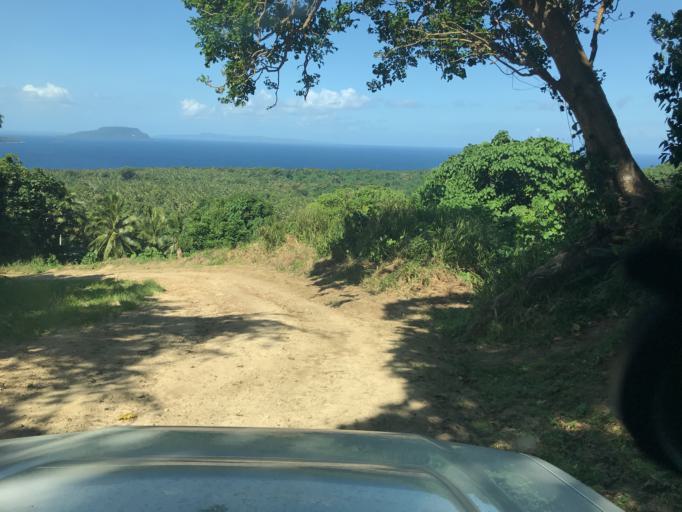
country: VU
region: Sanma
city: Luganville
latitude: -15.6456
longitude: 166.8331
